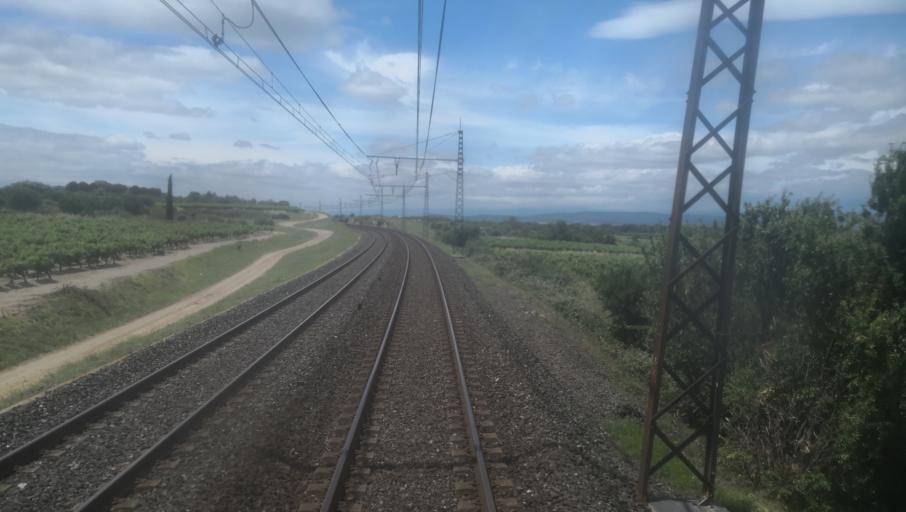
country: FR
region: Languedoc-Roussillon
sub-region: Departement de l'Aude
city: Nevian
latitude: 43.2120
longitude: 2.8934
